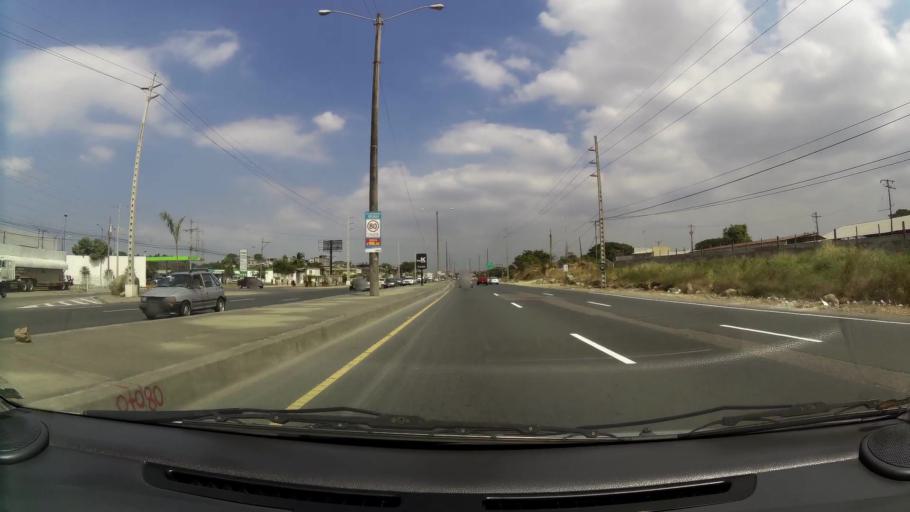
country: EC
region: Guayas
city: Eloy Alfaro
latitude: -2.0646
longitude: -79.9251
